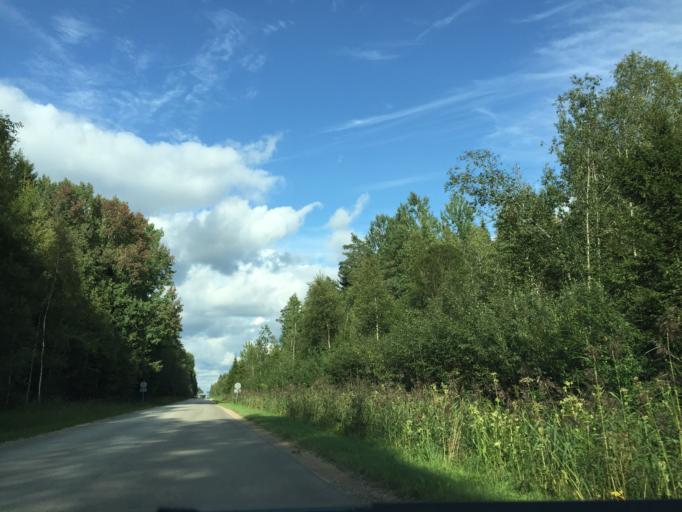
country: LV
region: Ogre
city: Ogre
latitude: 56.8365
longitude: 24.6591
